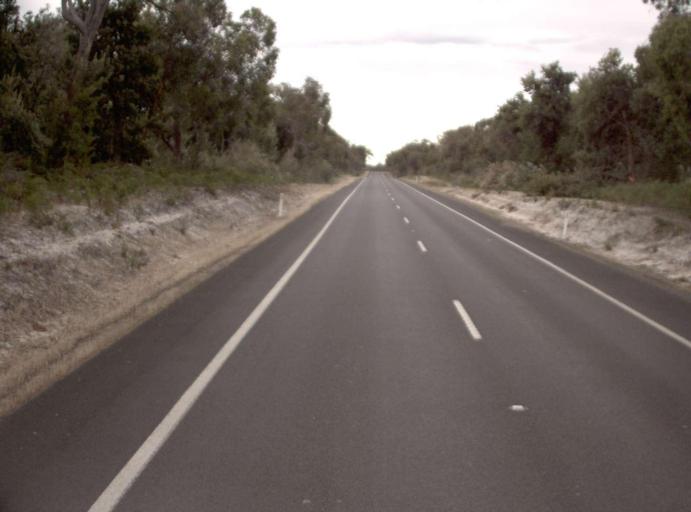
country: AU
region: Victoria
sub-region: Wellington
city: Sale
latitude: -38.3384
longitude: 147.0091
